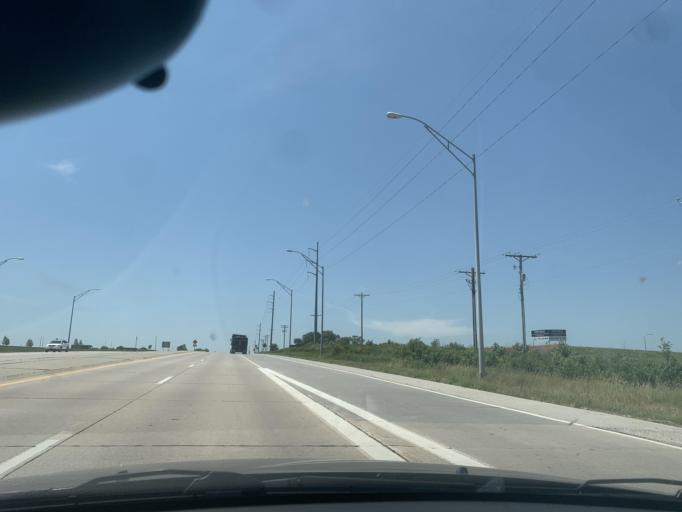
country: US
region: Nebraska
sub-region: Douglas County
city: Elkhorn
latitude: 41.2339
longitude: -96.2393
